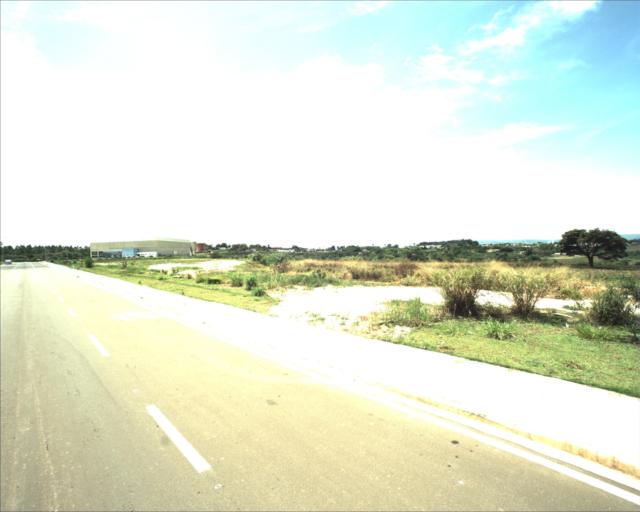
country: BR
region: Sao Paulo
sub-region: Sorocaba
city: Sorocaba
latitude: -23.5277
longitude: -47.5188
